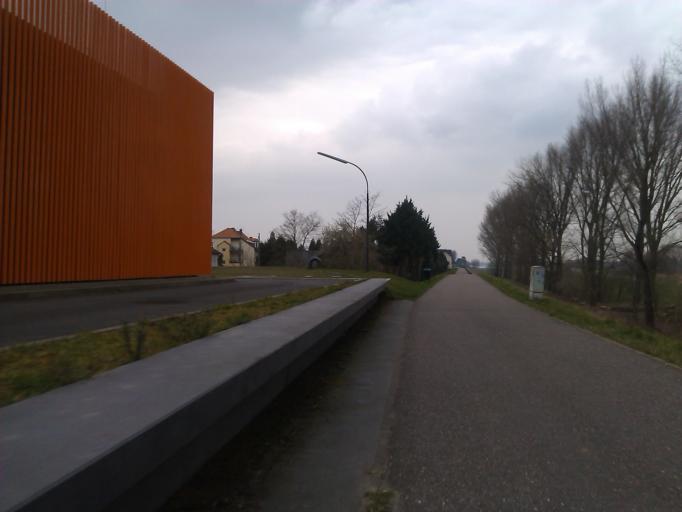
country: DE
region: North Rhine-Westphalia
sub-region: Regierungsbezirk Koln
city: Leverkusen
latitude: 51.0452
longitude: 6.9278
